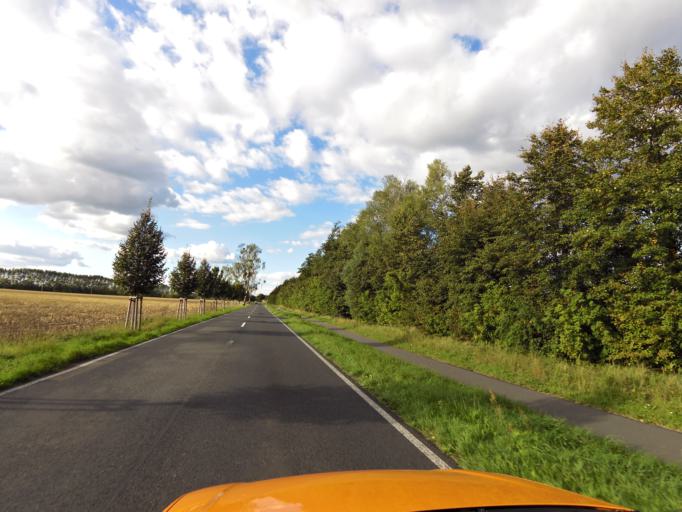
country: DE
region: Brandenburg
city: Trebbin
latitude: 52.1798
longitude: 13.1750
